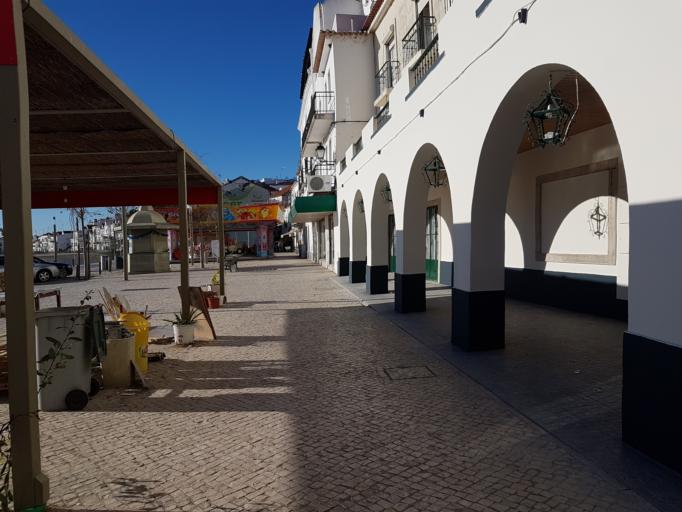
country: PT
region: Setubal
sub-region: Alcacer do Sal
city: Alcacer do Sal
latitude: 38.3712
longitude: -8.5069
